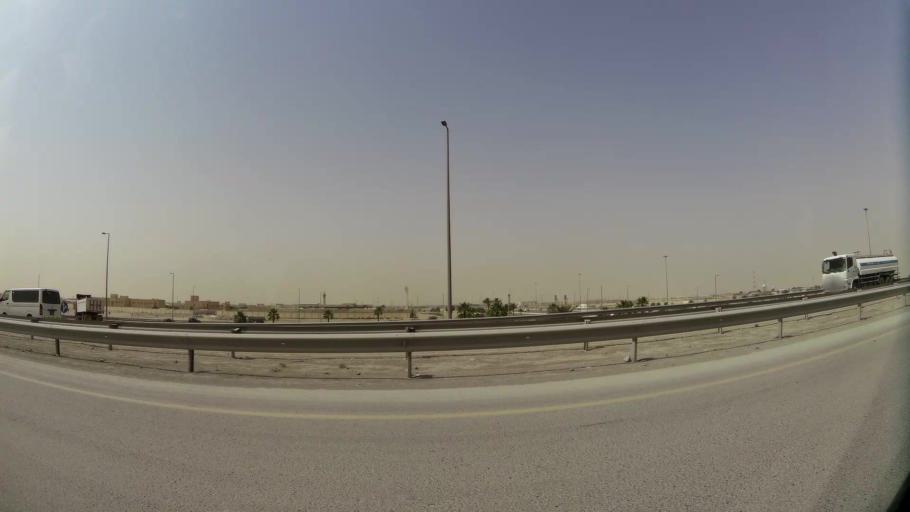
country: QA
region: Baladiyat ar Rayyan
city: Ar Rayyan
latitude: 25.2100
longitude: 51.4073
